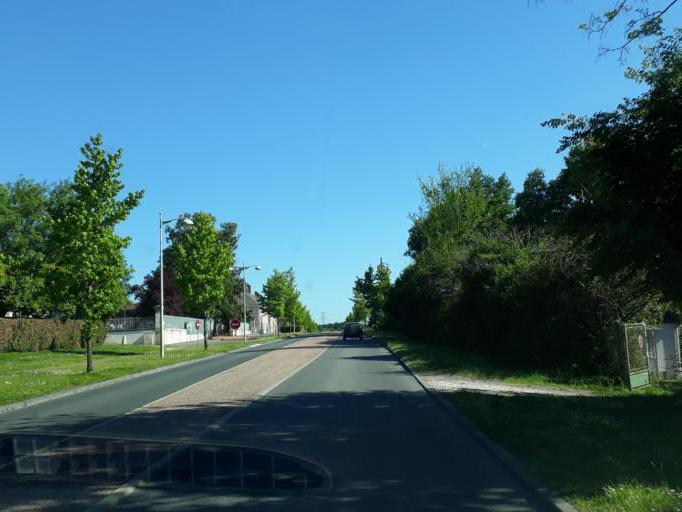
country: FR
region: Centre
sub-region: Departement du Cher
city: Lere
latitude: 47.4750
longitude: 2.9277
